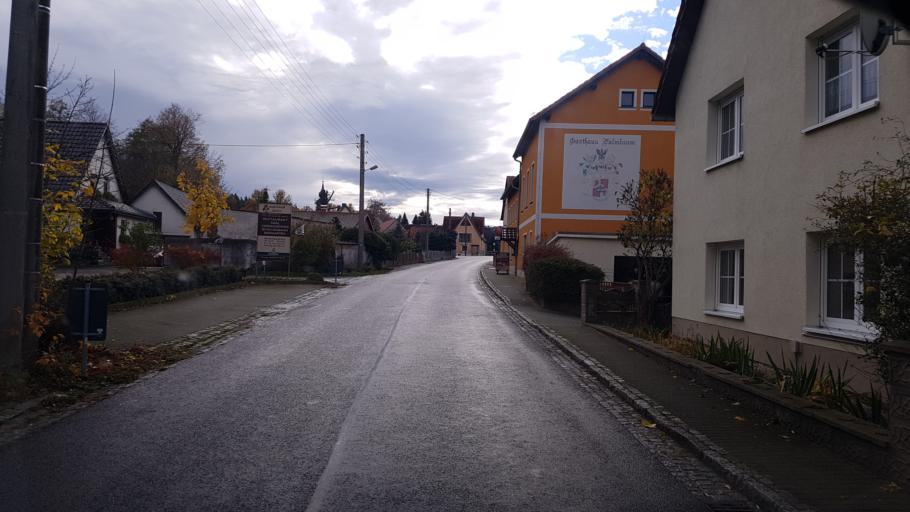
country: DE
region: Brandenburg
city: Grosskmehlen
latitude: 51.3443
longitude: 13.7347
